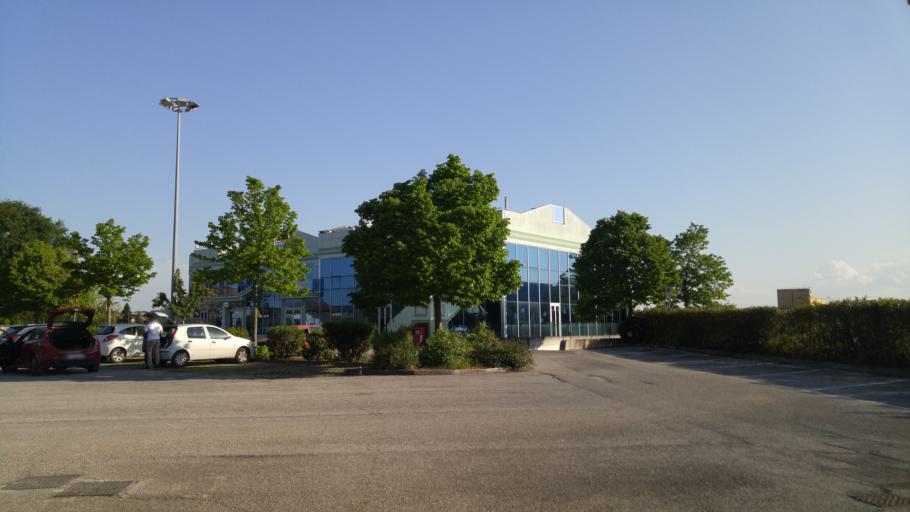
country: IT
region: The Marches
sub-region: Provincia di Pesaro e Urbino
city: Rosciano
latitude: 43.8219
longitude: 13.0086
